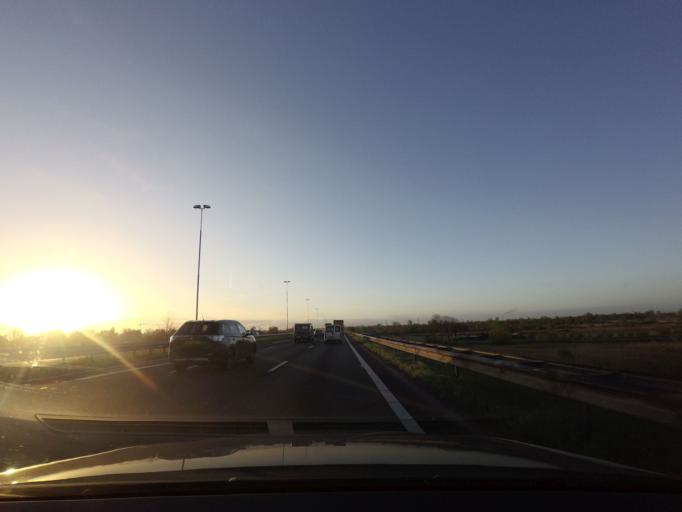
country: NL
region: North Holland
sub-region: Gemeente Zaanstad
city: Zaanstad
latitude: 52.4694
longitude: 4.7873
